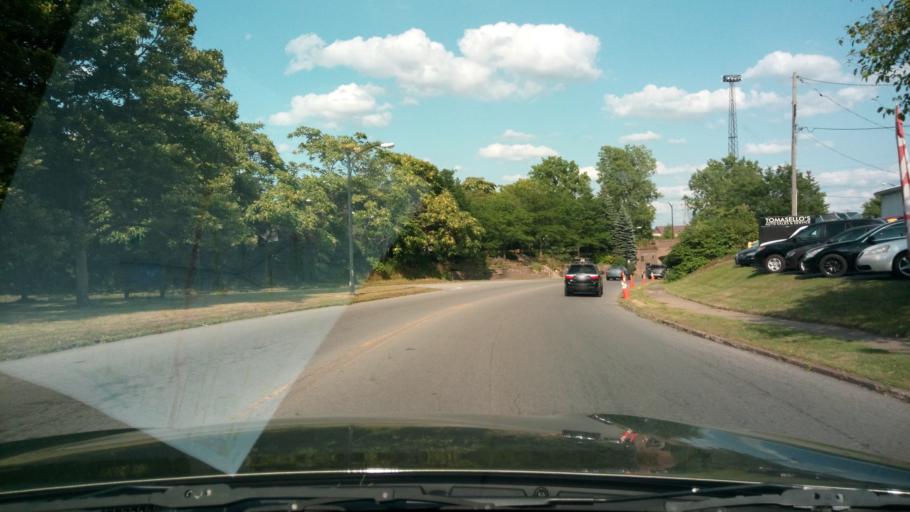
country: US
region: New York
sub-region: Erie County
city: Sloan
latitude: 42.8852
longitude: -78.8023
